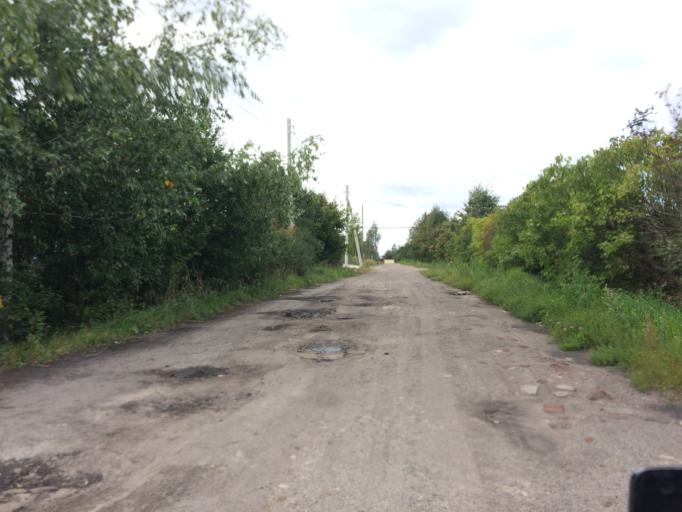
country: RU
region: Mariy-El
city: Yoshkar-Ola
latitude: 56.6612
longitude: 47.9938
